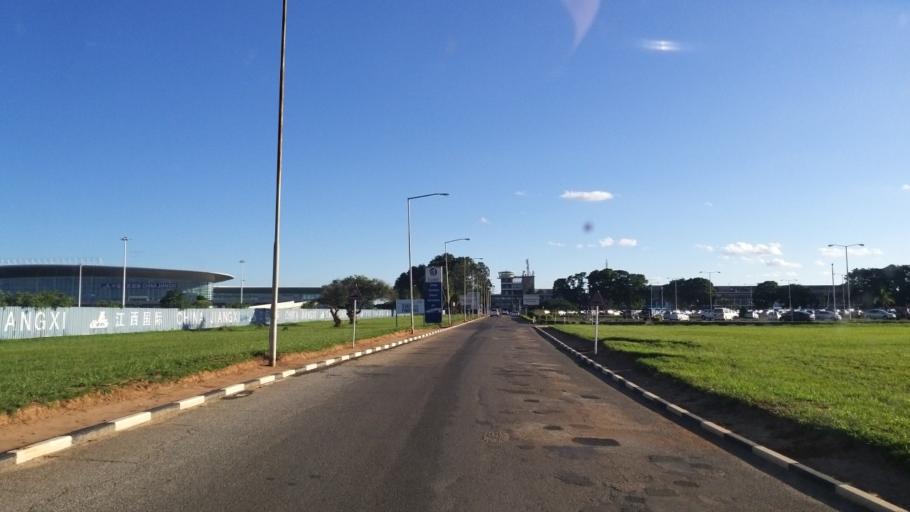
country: ZM
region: Lusaka
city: Lusaka
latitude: -15.3217
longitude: 28.4474
